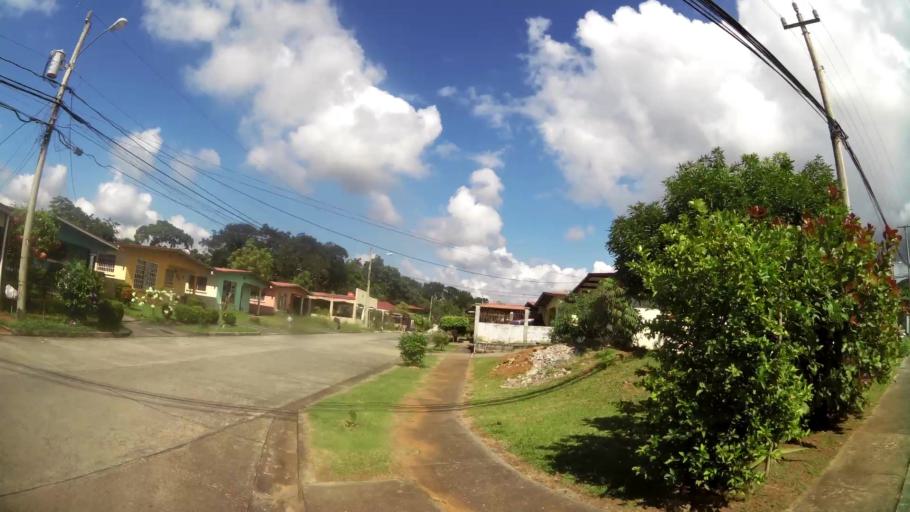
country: PA
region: Panama
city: Nuevo Arraijan
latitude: 8.9086
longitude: -79.7395
